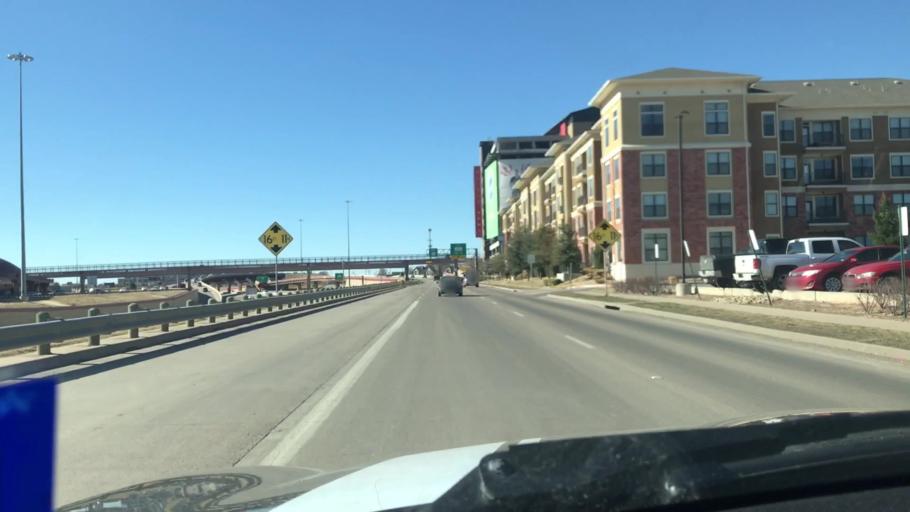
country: US
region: Texas
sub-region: Lubbock County
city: Lubbock
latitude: 33.5931
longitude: -101.8714
